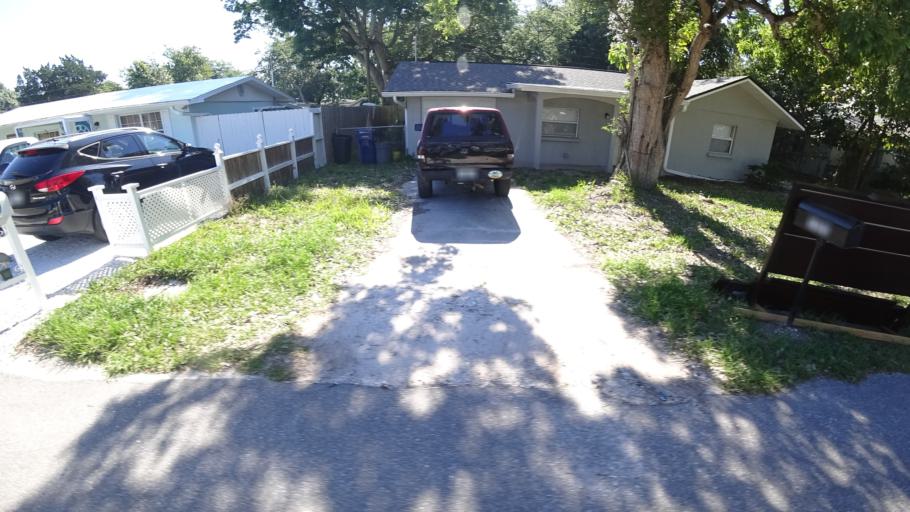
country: US
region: Florida
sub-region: Manatee County
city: West Bradenton
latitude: 27.4877
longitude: -82.5973
